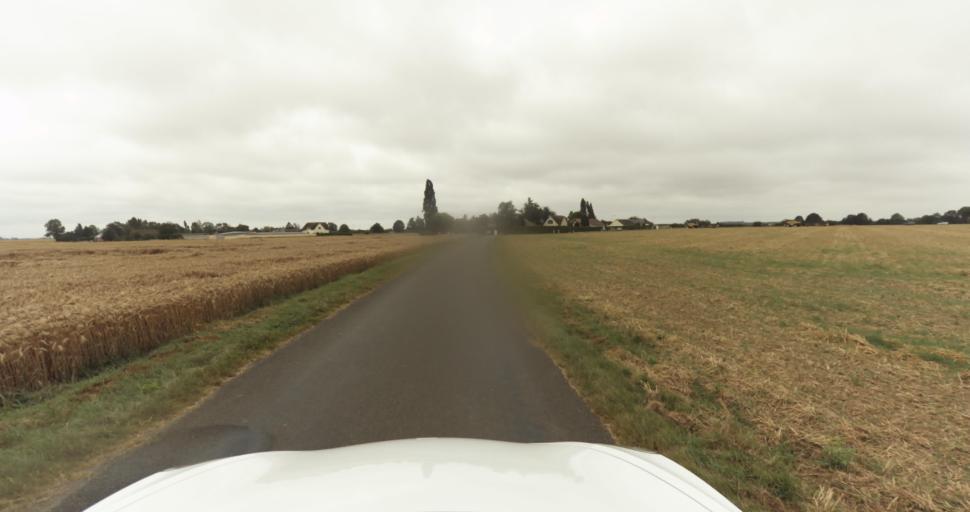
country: FR
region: Haute-Normandie
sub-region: Departement de l'Eure
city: Aviron
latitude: 49.0721
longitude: 1.0705
